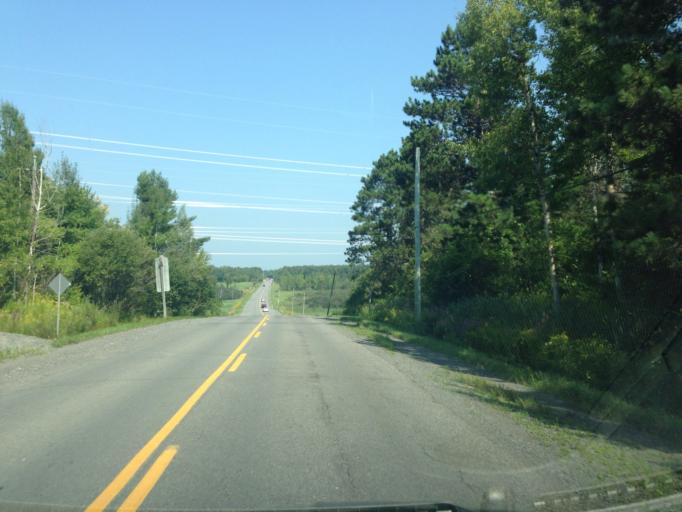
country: CA
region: Ontario
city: Ottawa
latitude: 45.4091
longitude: -75.5612
